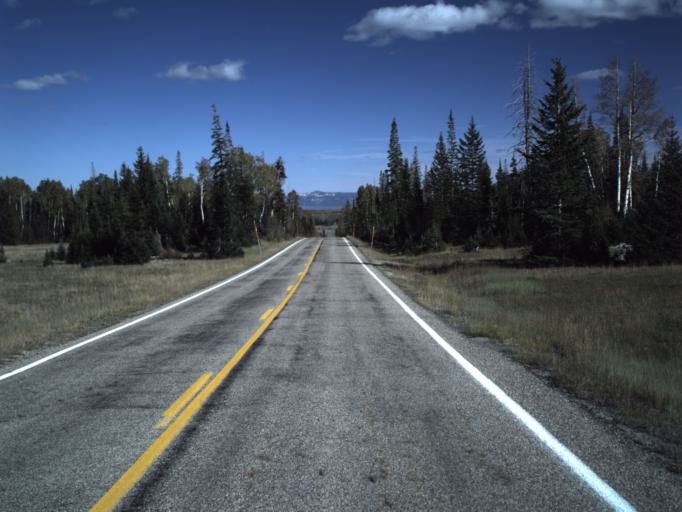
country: US
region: Utah
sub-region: Iron County
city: Parowan
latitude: 37.6530
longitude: -112.8030
